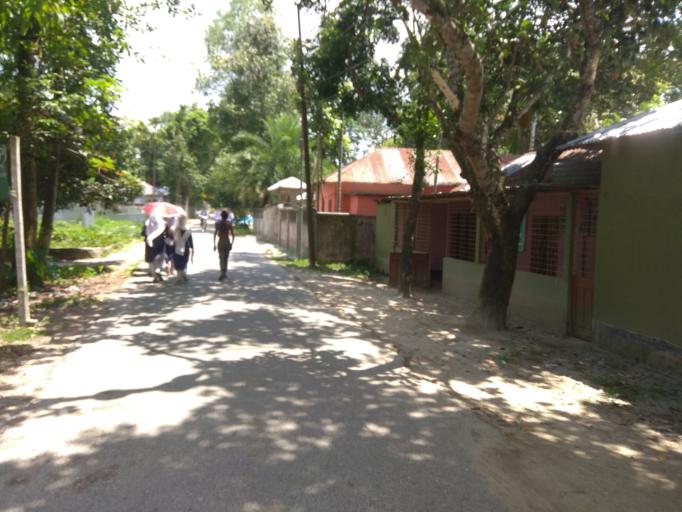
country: IN
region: West Bengal
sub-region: Koch Bihar
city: Haldibari
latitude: 26.1524
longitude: 88.9261
